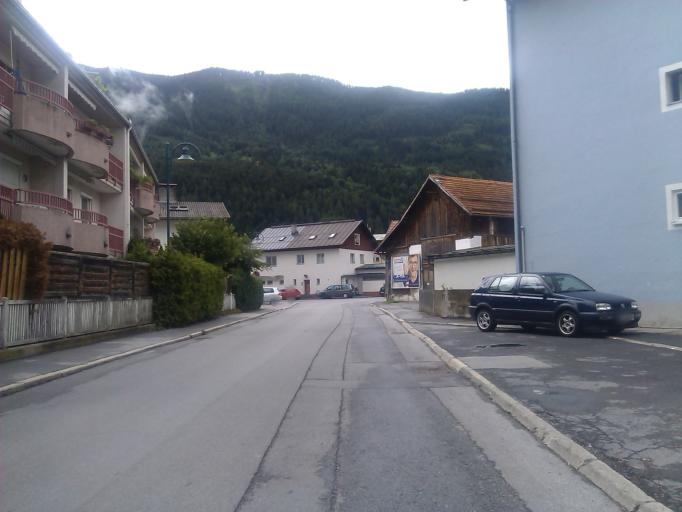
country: AT
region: Tyrol
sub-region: Politischer Bezirk Landeck
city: Landeck
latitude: 47.1497
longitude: 10.5703
